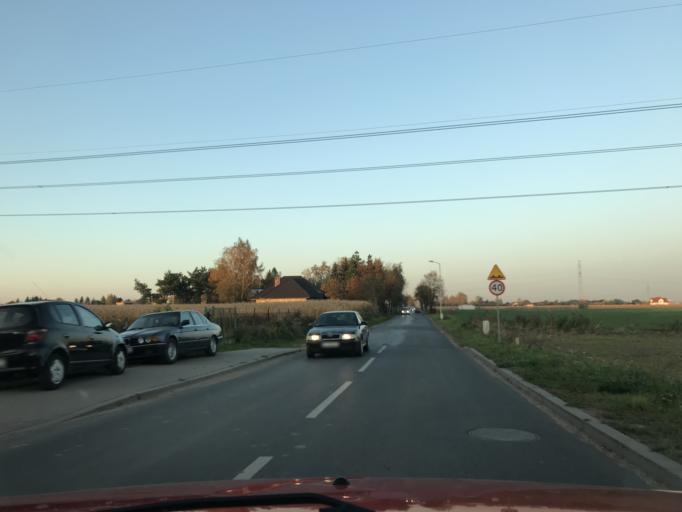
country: PL
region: Greater Poland Voivodeship
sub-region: Powiat poznanski
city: Baranowo
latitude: 52.3906
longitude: 16.7487
